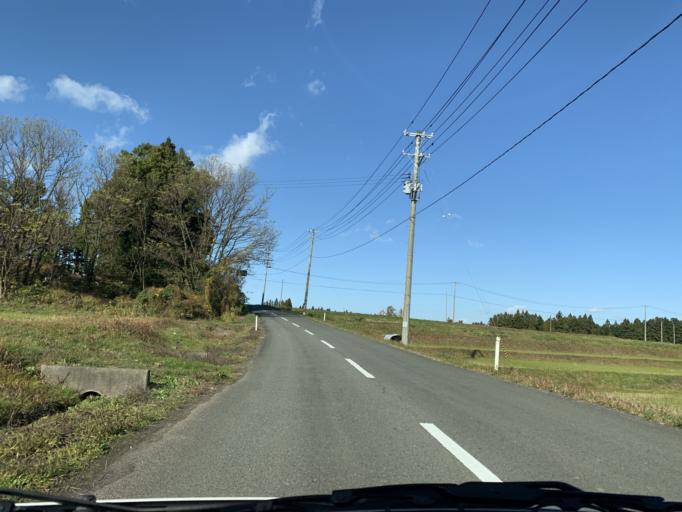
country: JP
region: Iwate
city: Mizusawa
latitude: 39.0654
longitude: 141.1126
